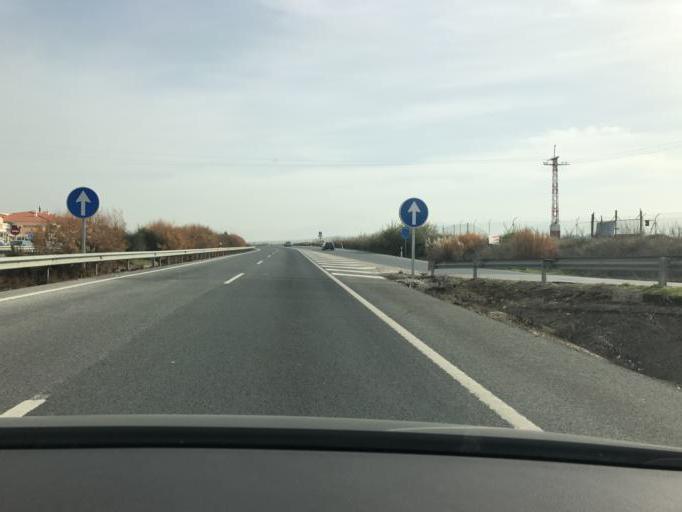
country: ES
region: Andalusia
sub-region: Provincia de Granada
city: Chauchina
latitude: 37.1907
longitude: -3.7771
